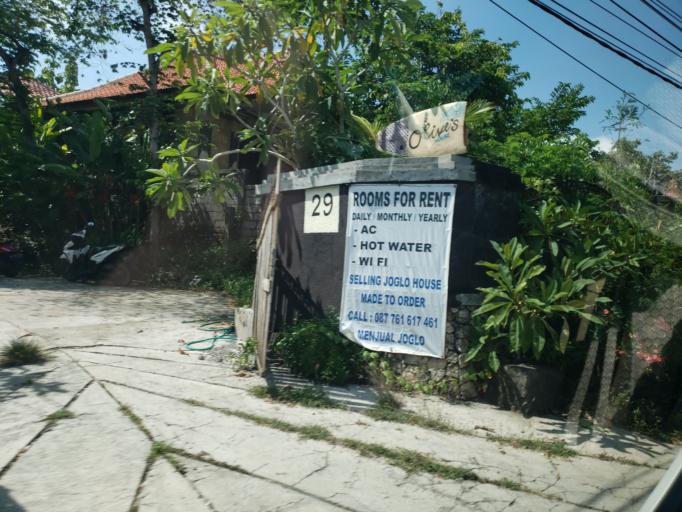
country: ID
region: Bali
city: Kangin
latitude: -8.8240
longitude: 115.1517
